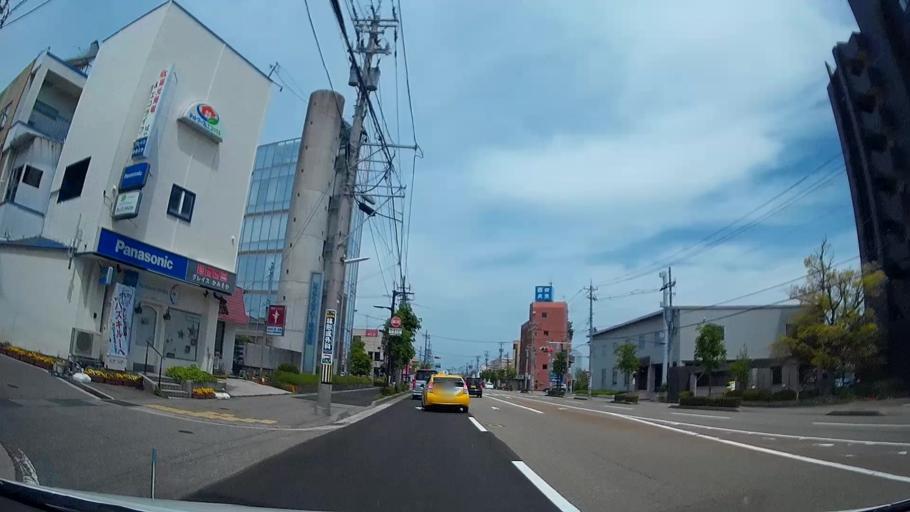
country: JP
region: Ishikawa
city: Kanazawa-shi
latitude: 36.5890
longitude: 136.6471
